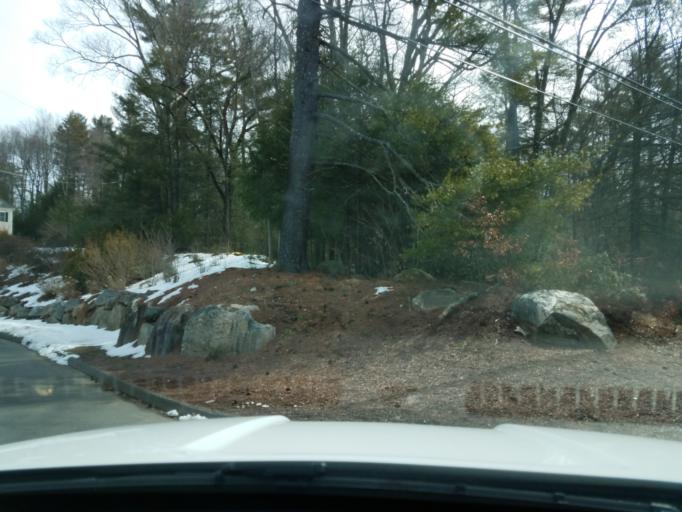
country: US
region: Connecticut
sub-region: Hartford County
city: Collinsville
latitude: 41.7855
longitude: -72.9208
